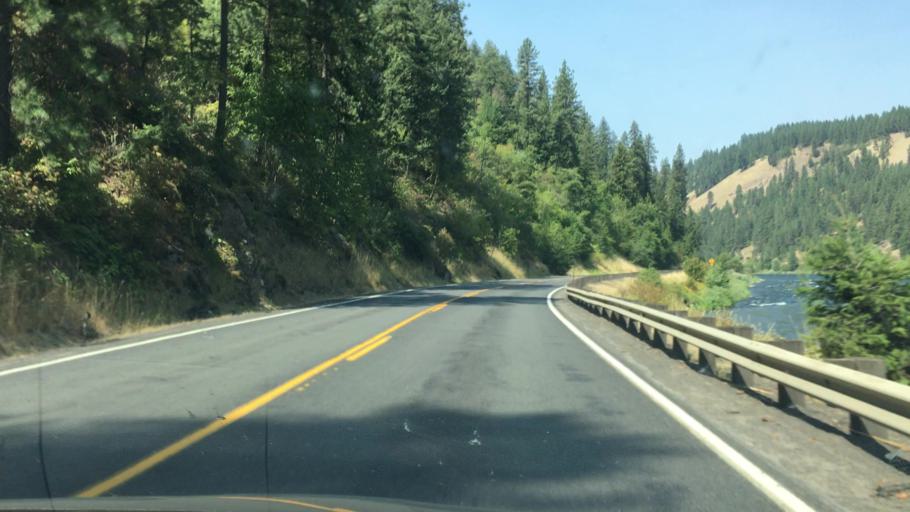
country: US
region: Idaho
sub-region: Clearwater County
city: Orofino
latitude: 46.4990
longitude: -116.3812
